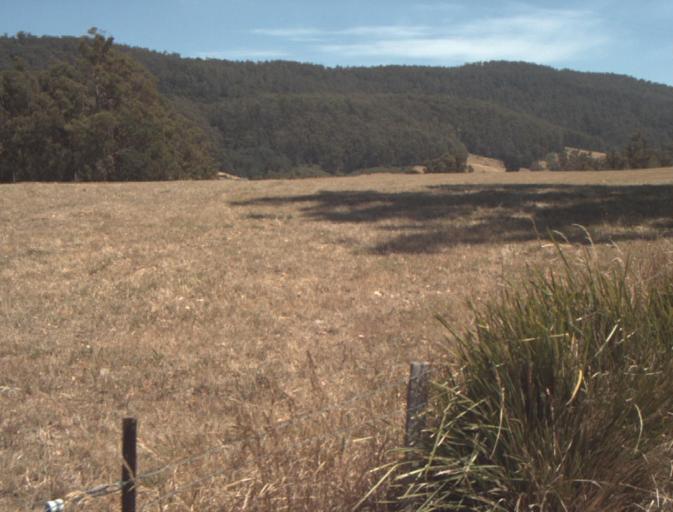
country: AU
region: Tasmania
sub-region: Launceston
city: Mayfield
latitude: -41.2432
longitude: 147.1302
